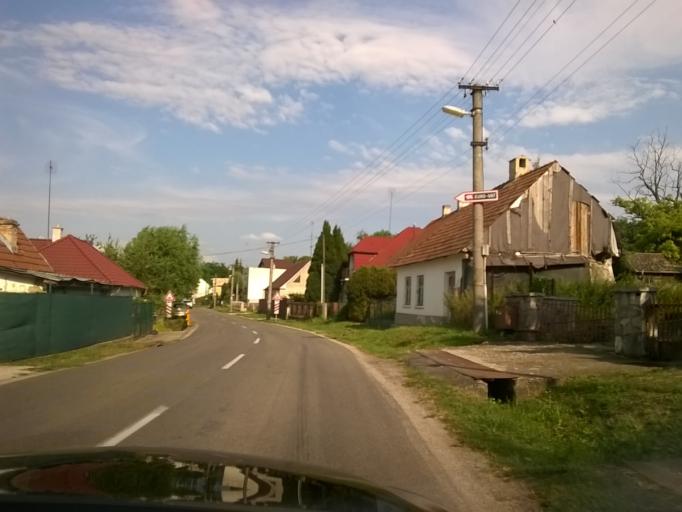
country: SK
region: Nitriansky
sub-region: Okres Nitra
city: Nitra
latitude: 48.3628
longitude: 17.9469
